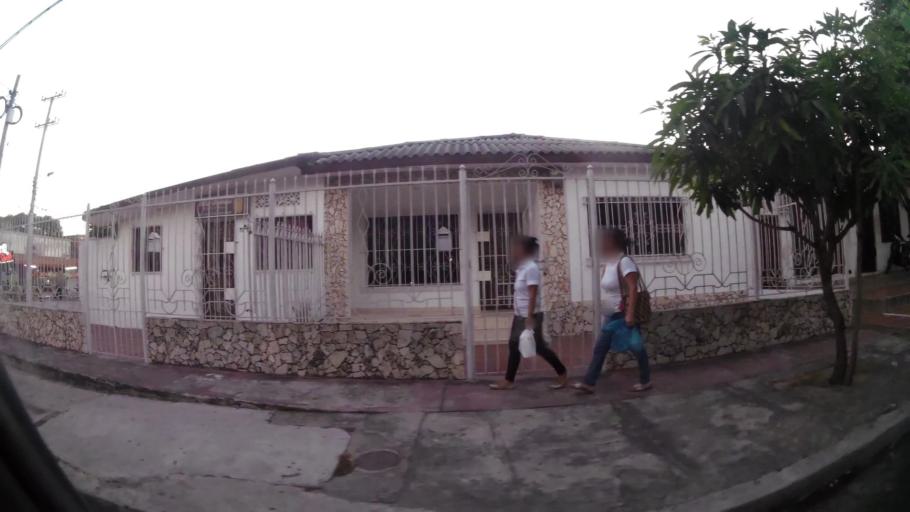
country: CO
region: Atlantico
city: Barranquilla
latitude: 10.9826
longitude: -74.8109
